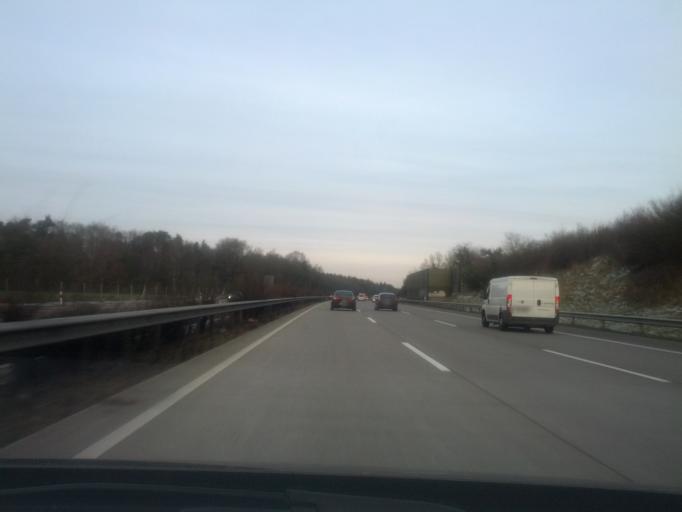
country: DE
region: Lower Saxony
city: Bispingen
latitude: 53.1340
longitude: 9.9955
